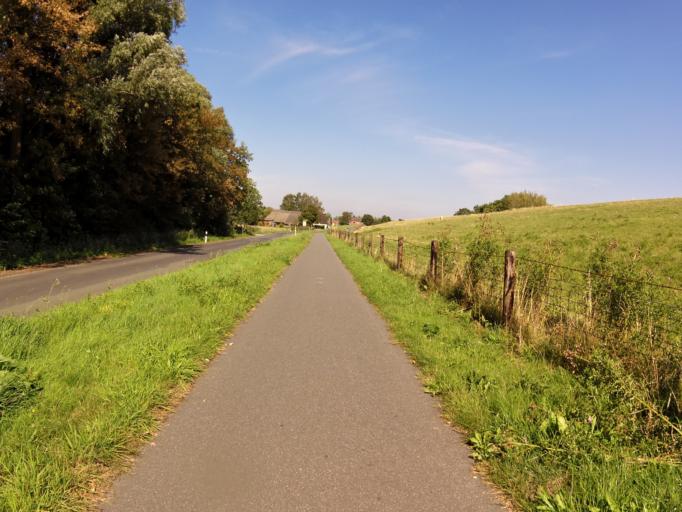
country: DE
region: Lower Saxony
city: Brake (Unterweser)
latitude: 53.2849
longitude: 8.4820
